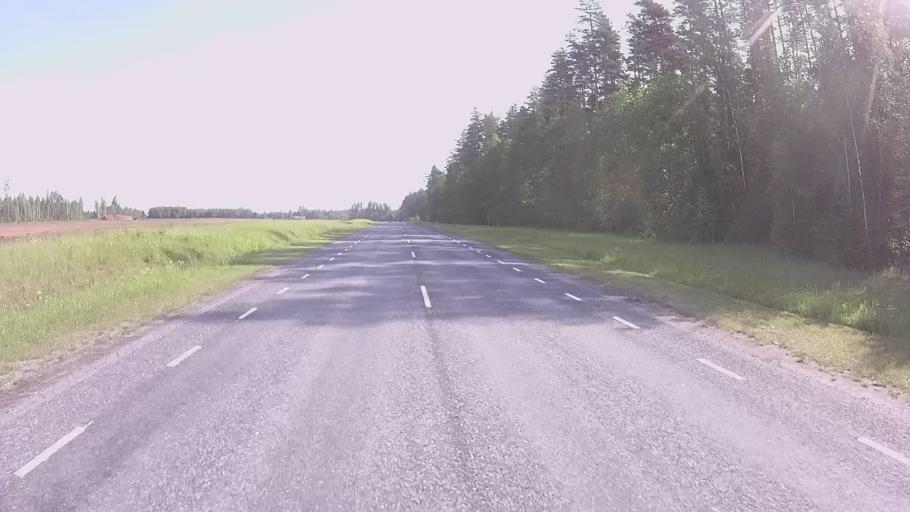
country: EE
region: Valgamaa
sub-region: Torva linn
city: Torva
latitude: 58.0284
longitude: 25.9646
